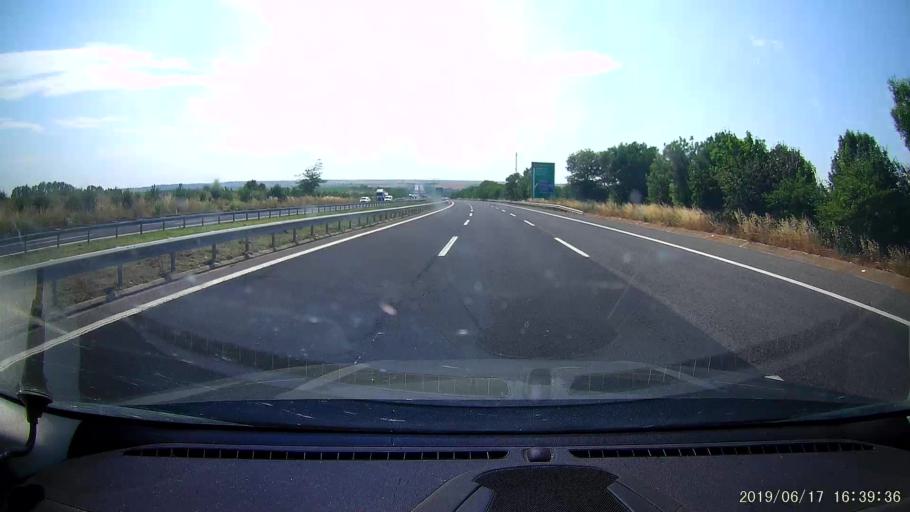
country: TR
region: Kirklareli
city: Luleburgaz
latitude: 41.4499
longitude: 27.4059
